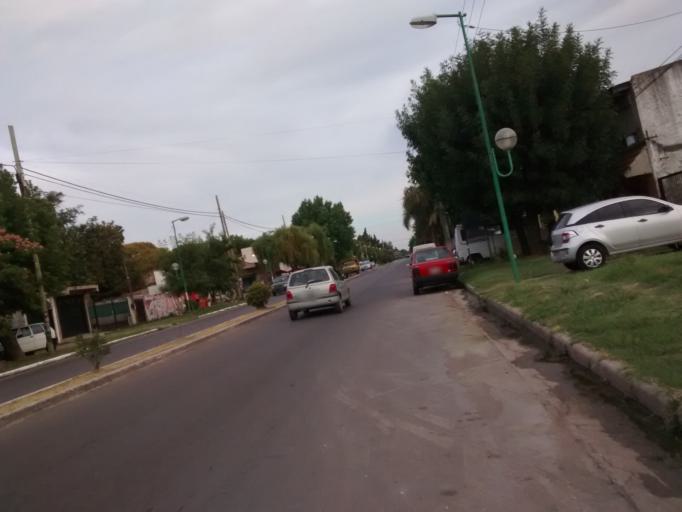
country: AR
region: Buenos Aires
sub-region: Partido de La Plata
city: La Plata
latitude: -34.9032
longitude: -58.0202
